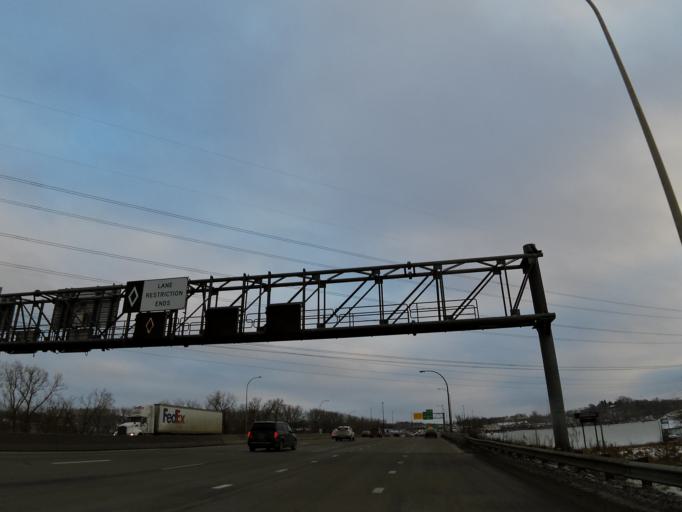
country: US
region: Minnesota
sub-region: Dakota County
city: Burnsville
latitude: 44.7828
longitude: -93.2887
